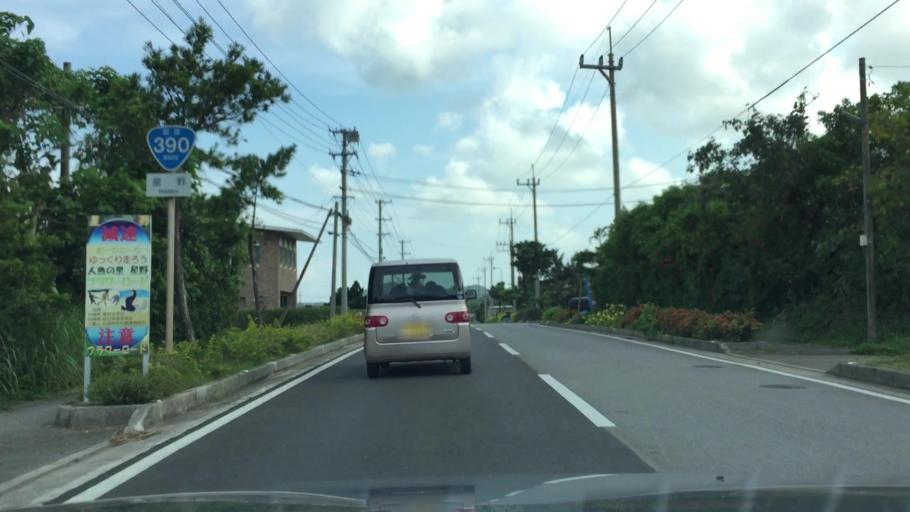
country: JP
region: Okinawa
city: Ishigaki
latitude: 24.4405
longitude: 124.2493
